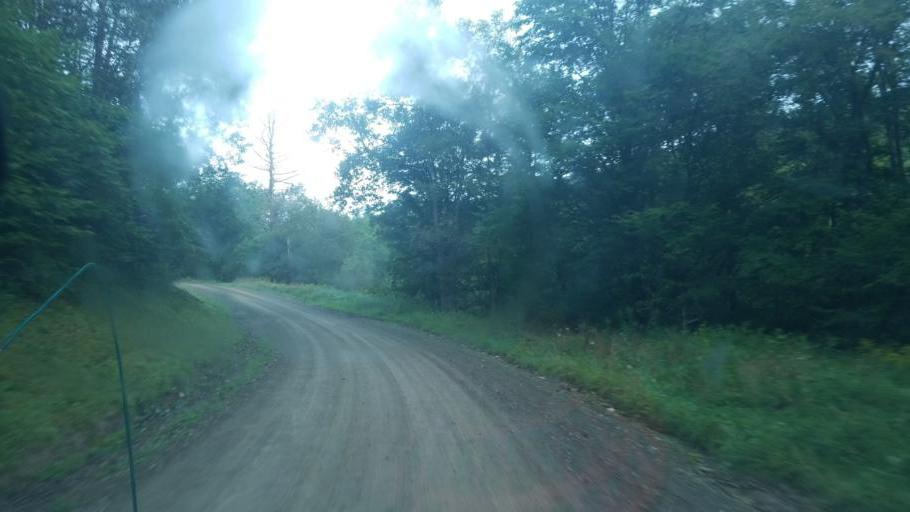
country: US
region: Pennsylvania
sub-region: Potter County
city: Galeton
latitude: 41.8490
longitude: -77.7934
